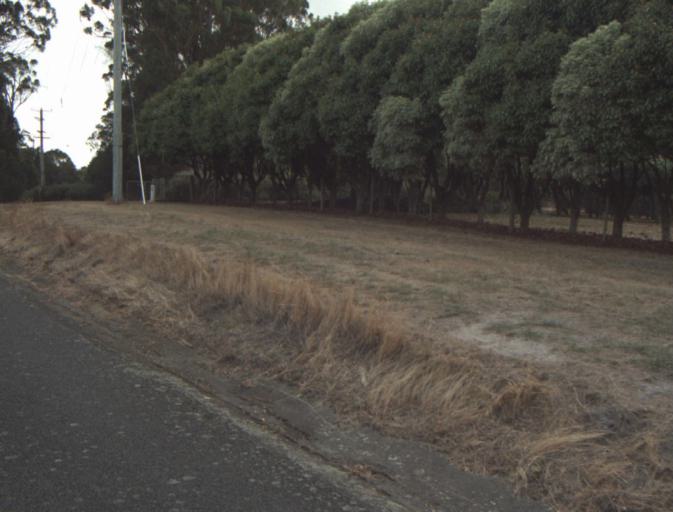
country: AU
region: Tasmania
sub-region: Launceston
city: Mayfield
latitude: -41.3296
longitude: 147.0581
